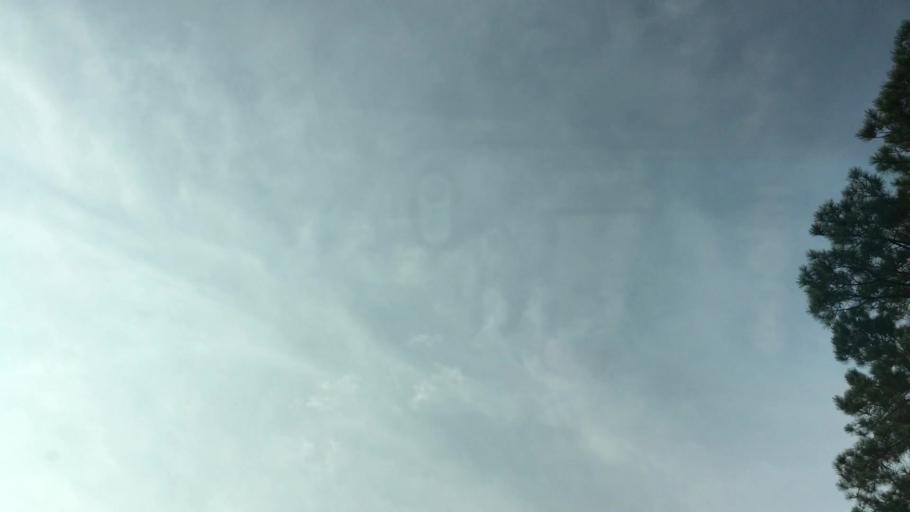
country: US
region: Alabama
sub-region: Bibb County
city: Woodstock
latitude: 33.2165
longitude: -87.1036
